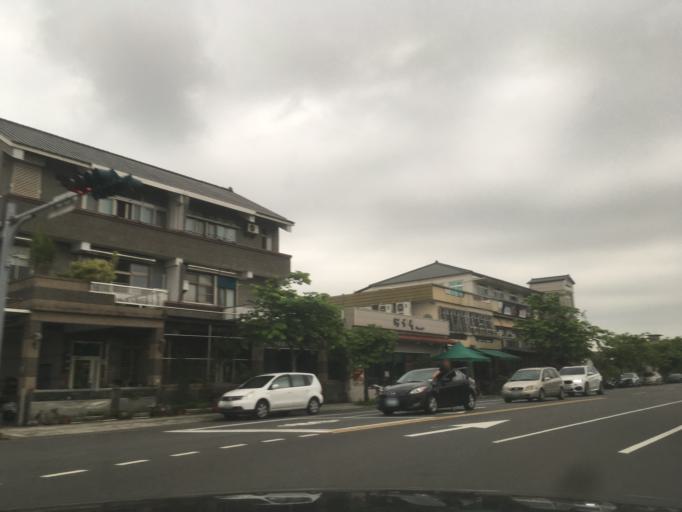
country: TW
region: Taiwan
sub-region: Yilan
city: Yilan
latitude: 24.7379
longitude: 121.7501
